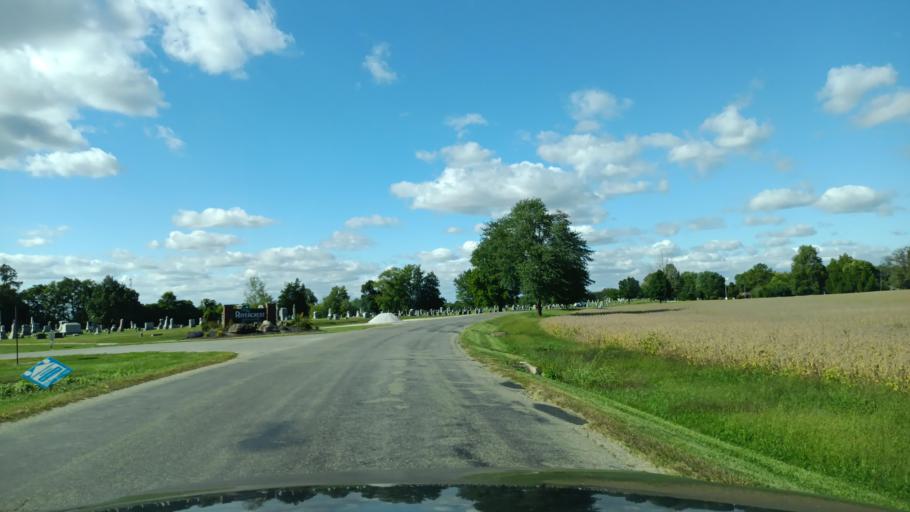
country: US
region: Indiana
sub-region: Fountain County
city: Covington
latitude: 40.1280
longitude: -87.3853
